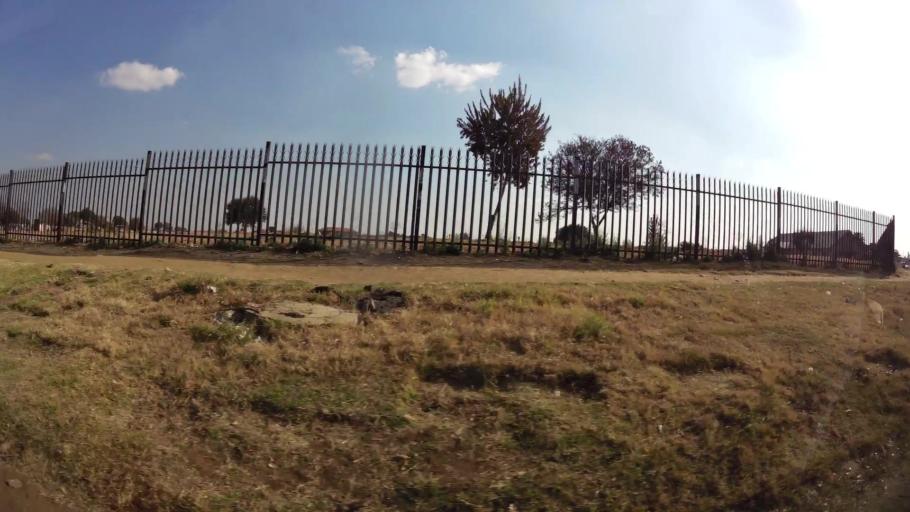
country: ZA
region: Gauteng
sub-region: Ekurhuleni Metropolitan Municipality
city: Brakpan
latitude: -26.1528
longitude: 28.4086
